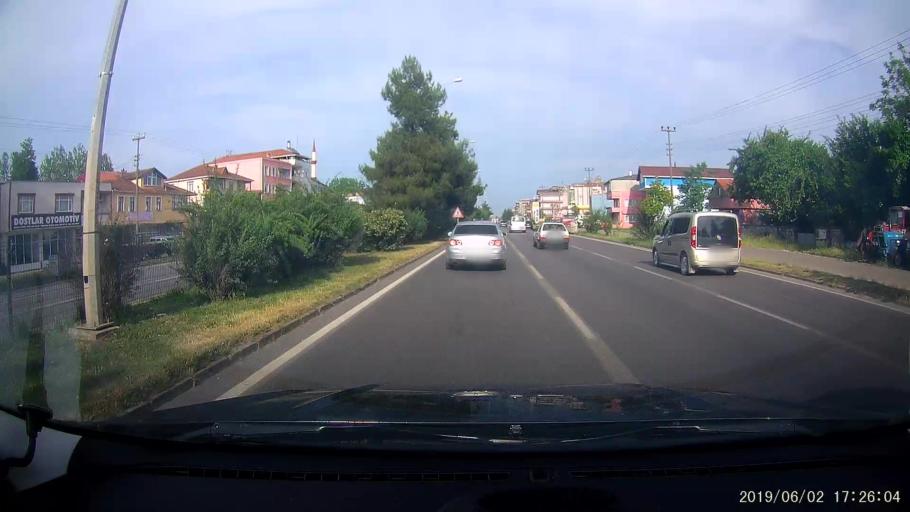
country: TR
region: Samsun
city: Carsamba
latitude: 41.2044
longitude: 36.7153
